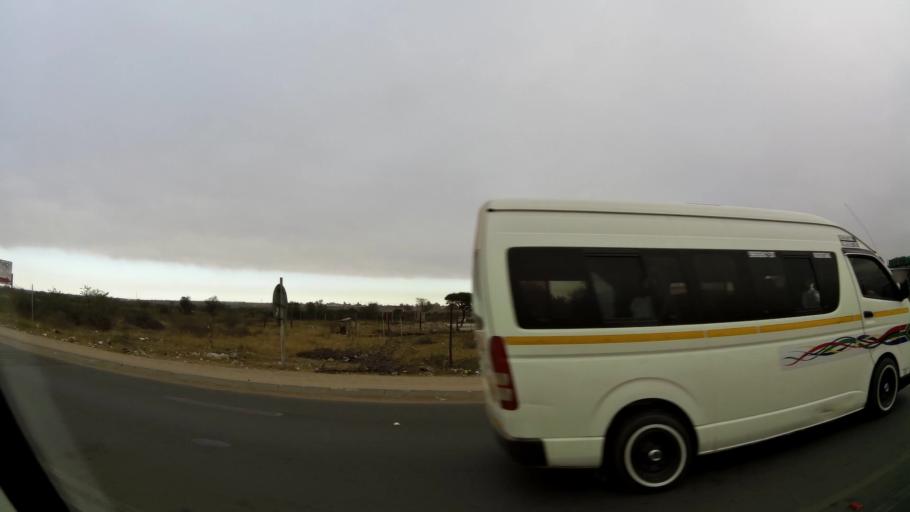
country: ZA
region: Limpopo
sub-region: Capricorn District Municipality
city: Polokwane
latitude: -23.8298
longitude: 29.3797
